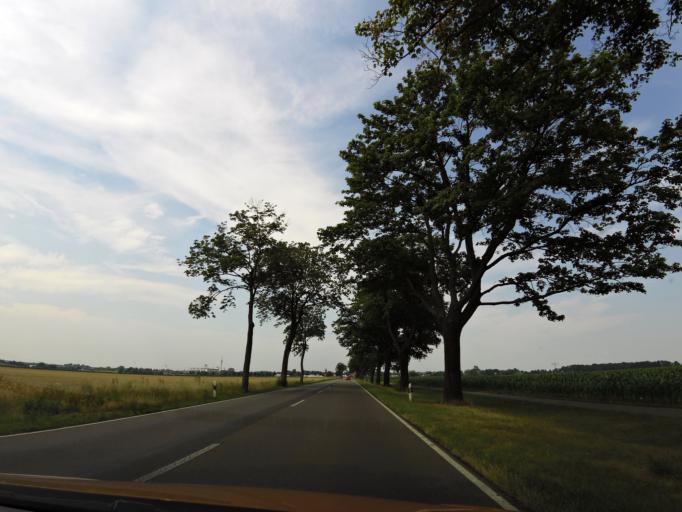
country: DE
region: Brandenburg
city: Kyritz
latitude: 52.9292
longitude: 12.4168
